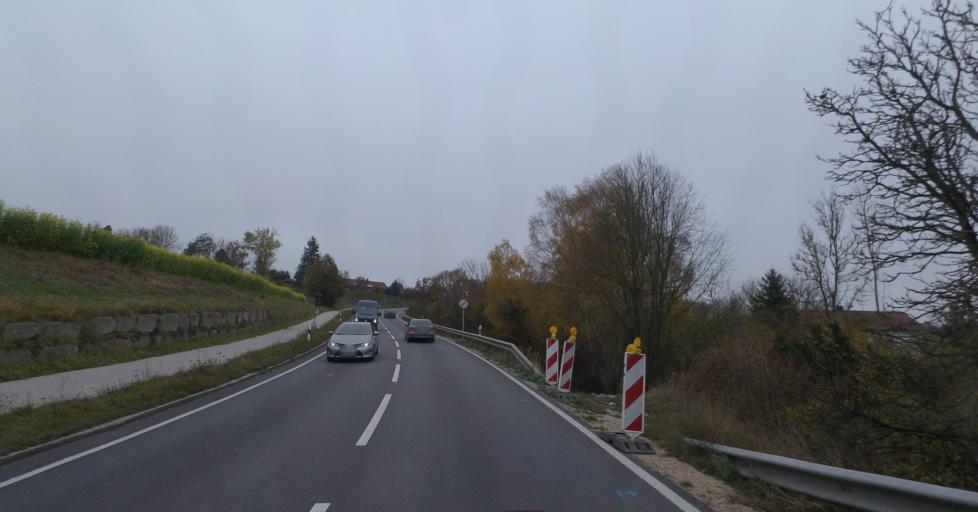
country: DE
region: Bavaria
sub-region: Upper Bavaria
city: Garching an der Alz
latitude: 48.1222
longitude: 12.5757
